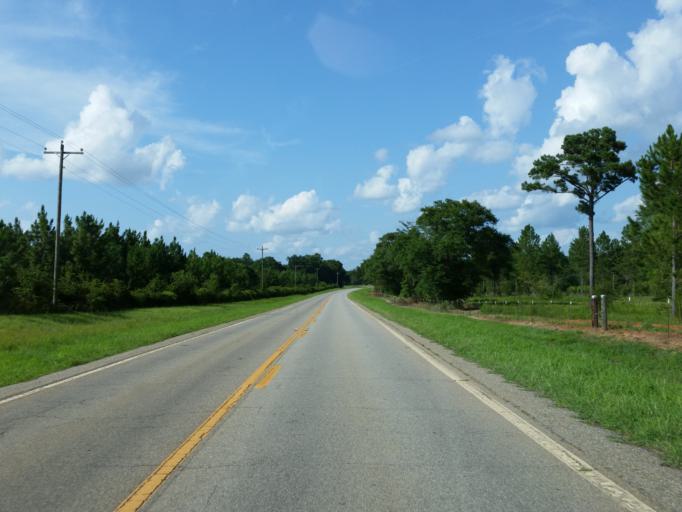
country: US
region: Georgia
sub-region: Lee County
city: Leesburg
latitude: 31.8101
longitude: -84.1164
